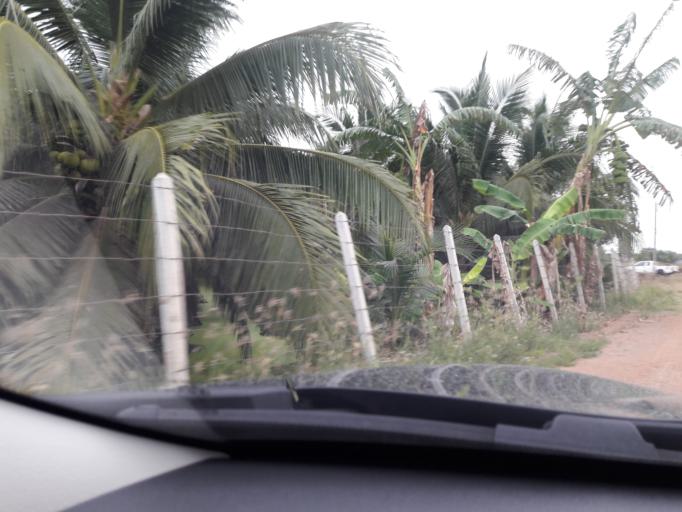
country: TH
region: Ratchaburi
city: Bang Phae
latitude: 13.6177
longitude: 99.9633
